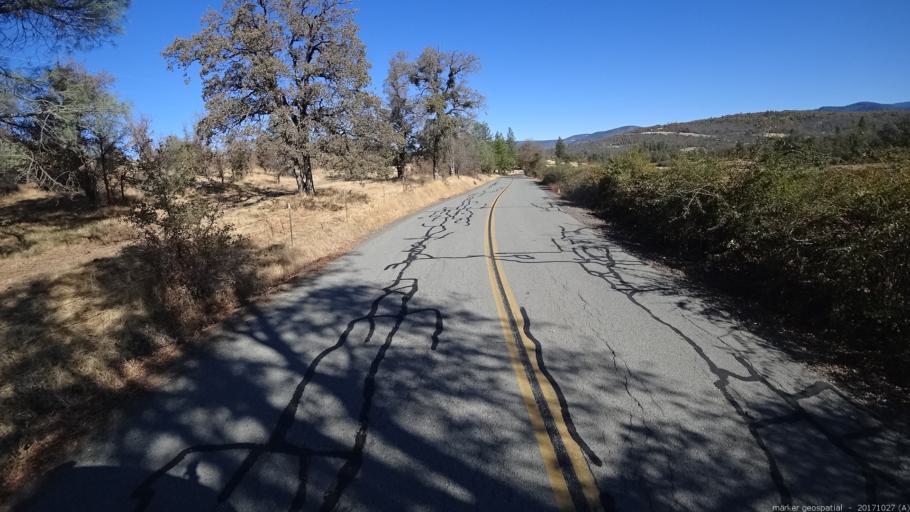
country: US
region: California
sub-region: Shasta County
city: Shingletown
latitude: 40.7684
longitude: -121.9702
